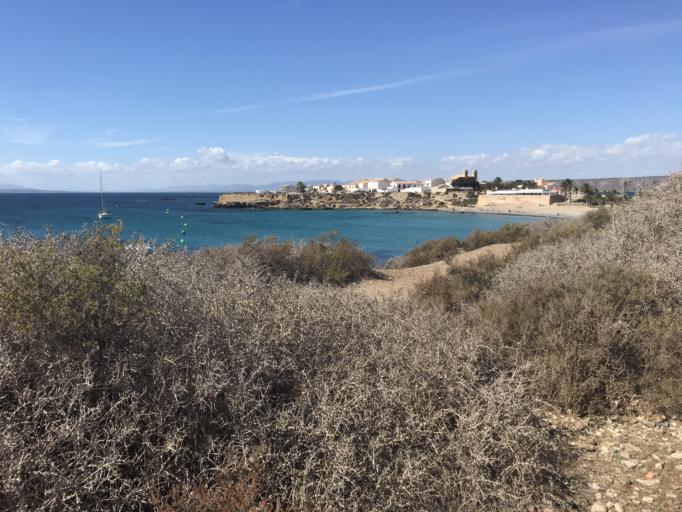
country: ES
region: Valencia
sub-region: Provincia de Alicante
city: Santa Pola
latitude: 38.1643
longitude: -0.4772
